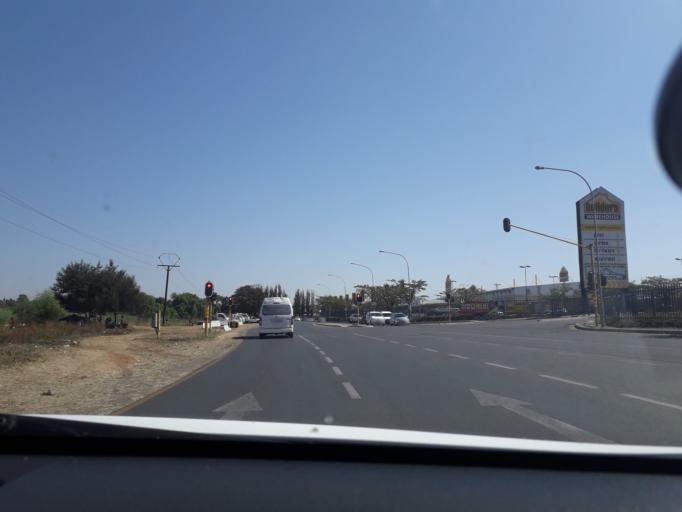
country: ZA
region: Gauteng
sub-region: City of Johannesburg Metropolitan Municipality
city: Modderfontein
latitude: -26.0985
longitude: 28.2206
